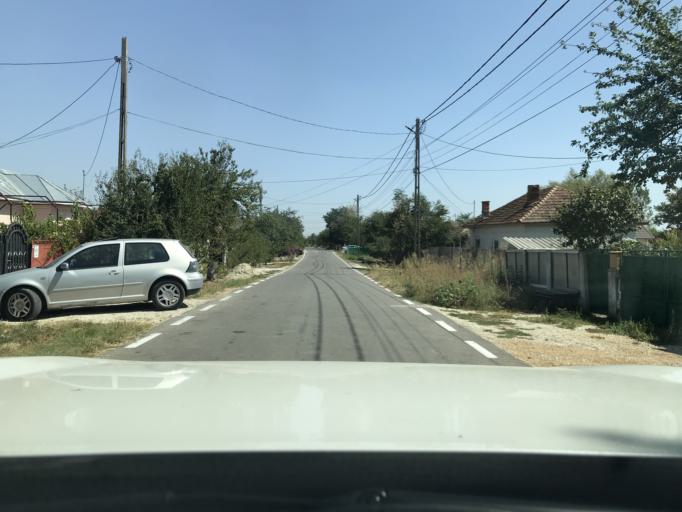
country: RO
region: Olt
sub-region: Comuna Falcoiu
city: Falcoiu
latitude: 44.2438
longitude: 24.3590
